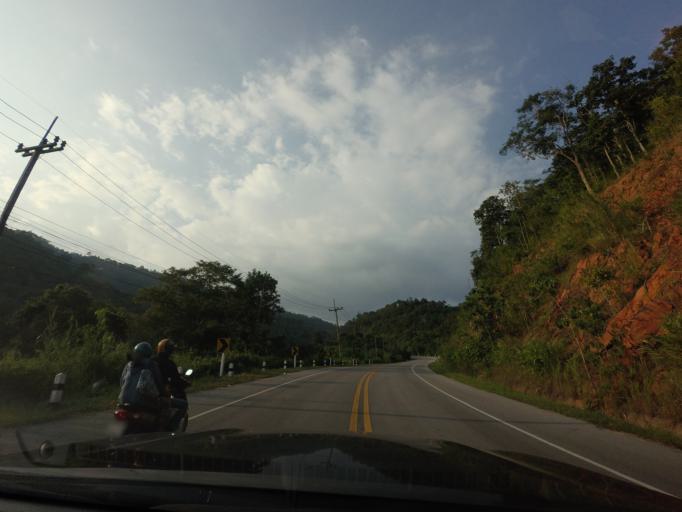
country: TH
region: Loei
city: Dan Sai
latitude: 17.3076
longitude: 101.1261
